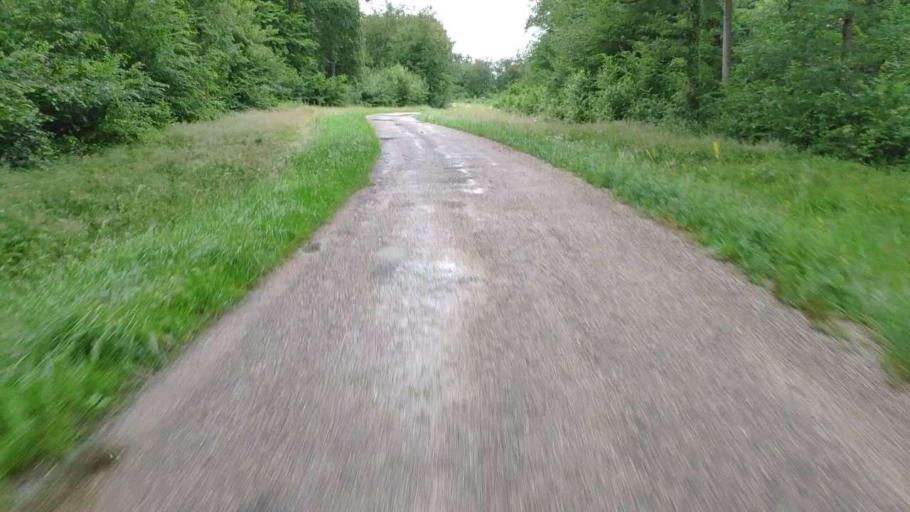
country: FR
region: Franche-Comte
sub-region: Departement du Jura
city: Chaussin
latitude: 46.8865
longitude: 5.4209
